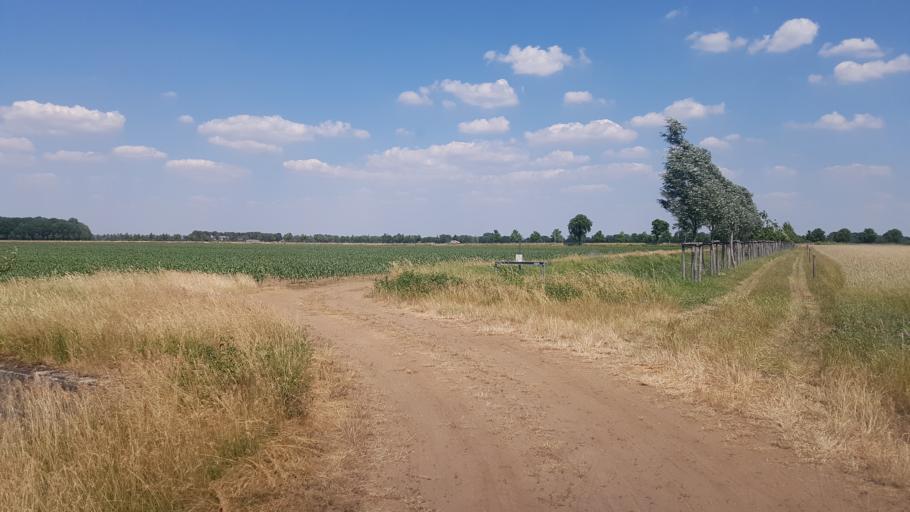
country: DE
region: Brandenburg
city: Herzberg
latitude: 51.6717
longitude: 13.2630
